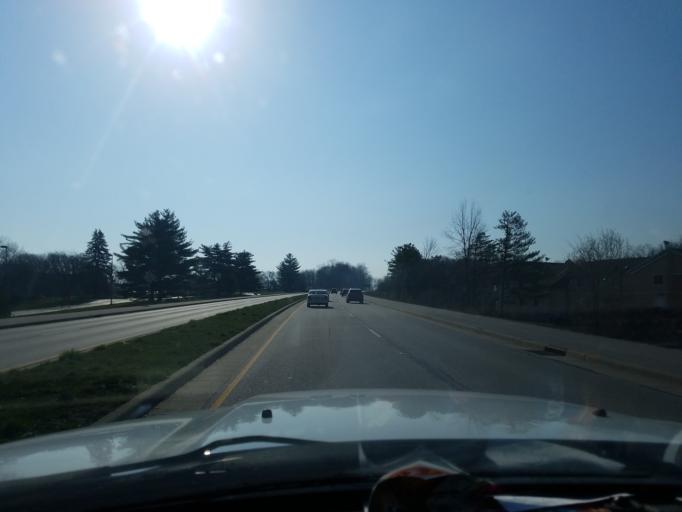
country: US
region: Indiana
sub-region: Monroe County
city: Bloomington
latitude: 39.1846
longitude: -86.5146
